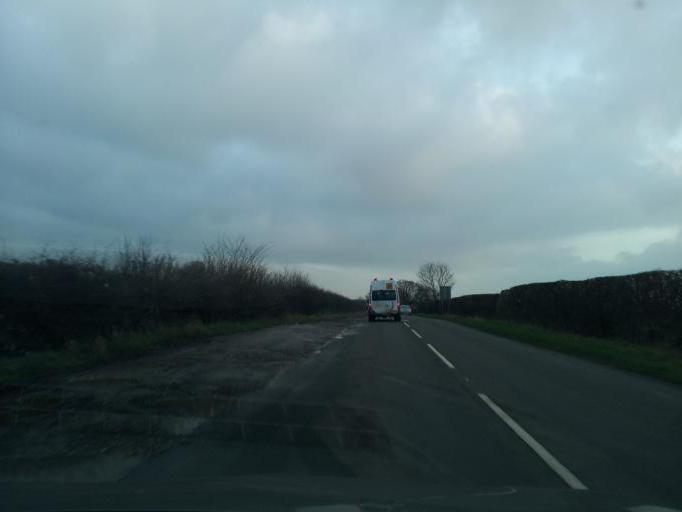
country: GB
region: England
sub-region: Derbyshire
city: Etwall
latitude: 52.8586
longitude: -1.5986
